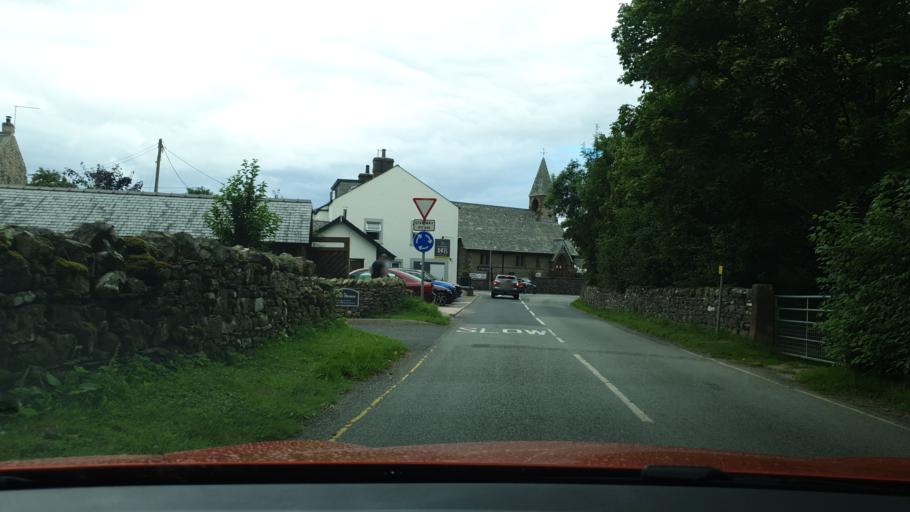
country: GB
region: England
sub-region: Cumbria
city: Penrith
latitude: 54.6129
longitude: -2.8168
